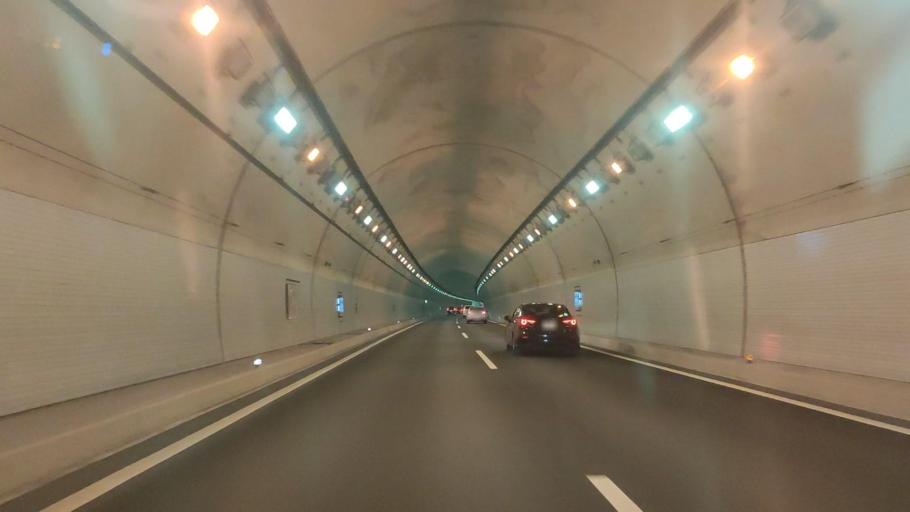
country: JP
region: Fukuoka
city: Kanda
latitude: 33.8067
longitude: 130.9194
